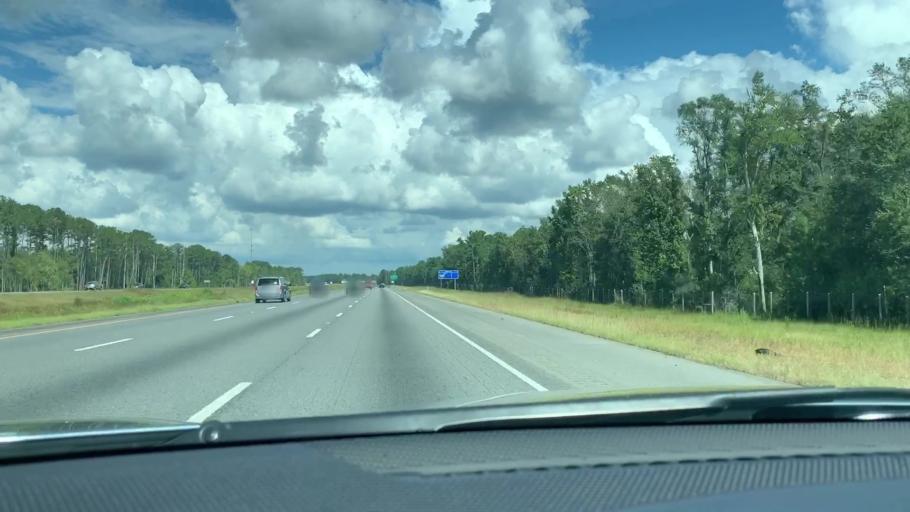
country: US
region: Georgia
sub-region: Glynn County
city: Brunswick
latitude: 31.0815
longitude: -81.6133
